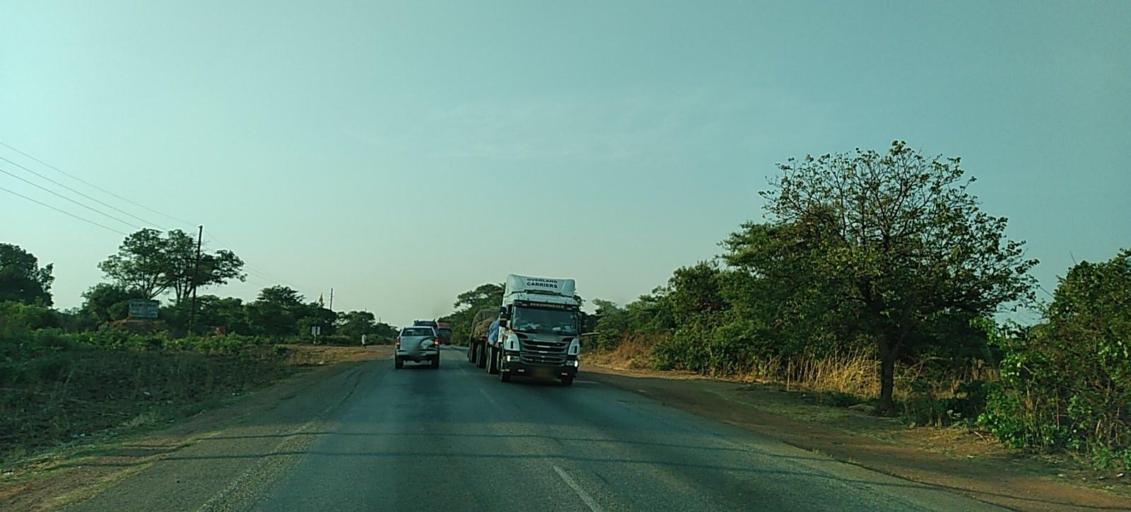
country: ZM
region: Copperbelt
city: Ndola
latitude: -13.1547
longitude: 28.6987
